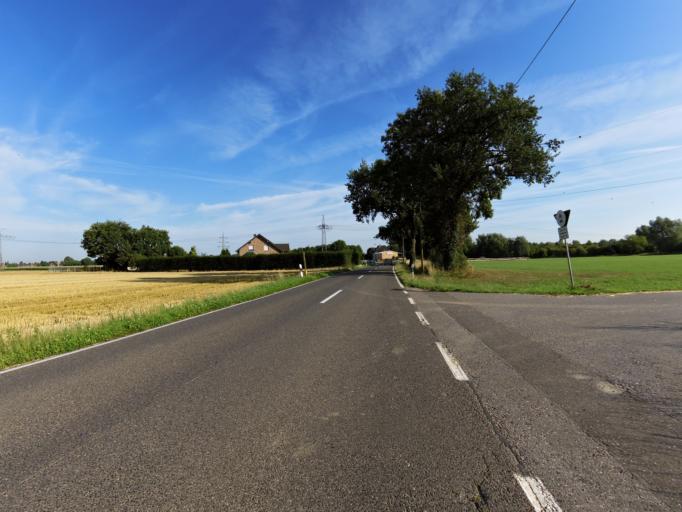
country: DE
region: North Rhine-Westphalia
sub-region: Regierungsbezirk Koln
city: Wassenberg
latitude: 51.0515
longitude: 6.1734
